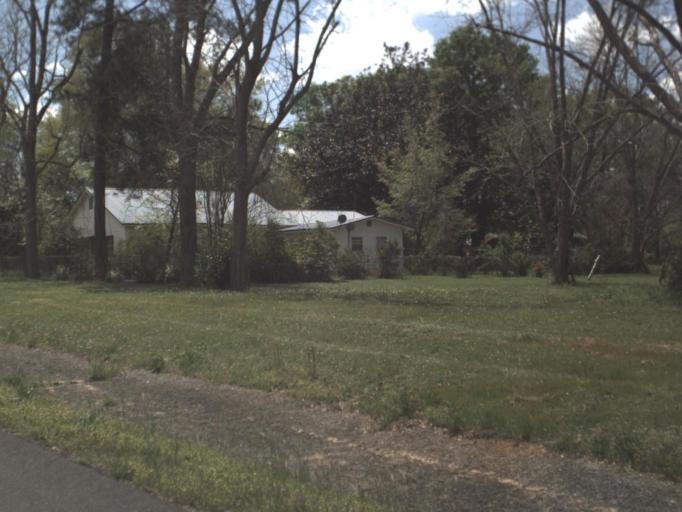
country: US
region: Florida
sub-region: Okaloosa County
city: Crestview
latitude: 30.8481
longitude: -86.6751
